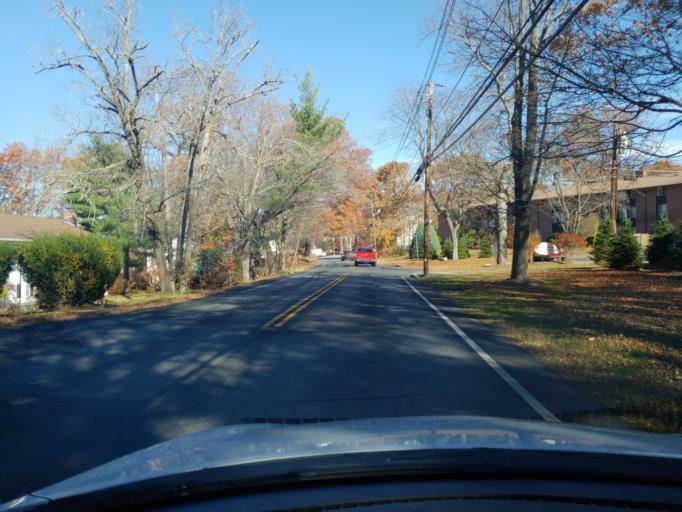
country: US
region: Massachusetts
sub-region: Essex County
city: Andover
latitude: 42.6728
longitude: -71.1359
